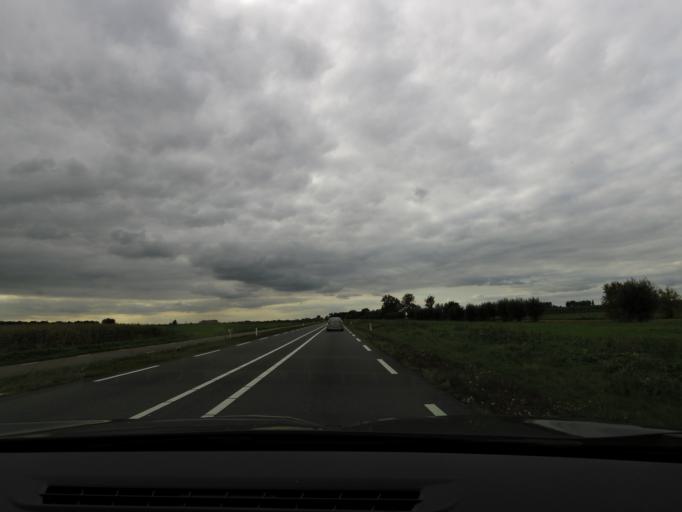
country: NL
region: South Holland
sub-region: Molenwaard
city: Liesveld
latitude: 51.9278
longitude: 4.7614
